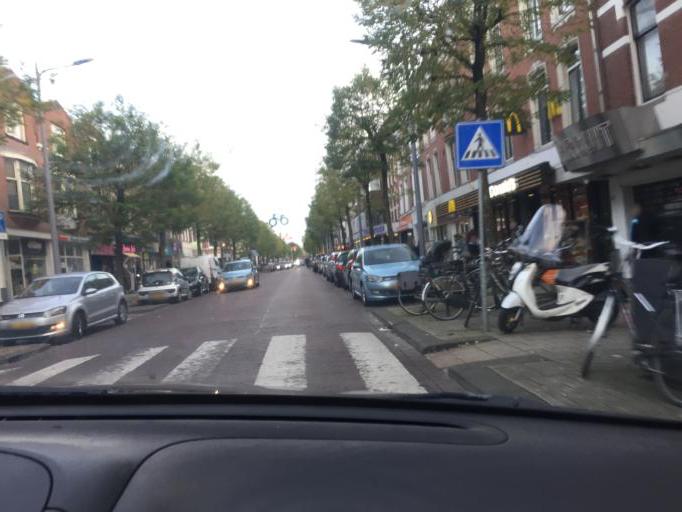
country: NL
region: South Holland
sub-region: Gemeente Rotterdam
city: Rotterdam
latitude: 51.9335
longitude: 4.4777
